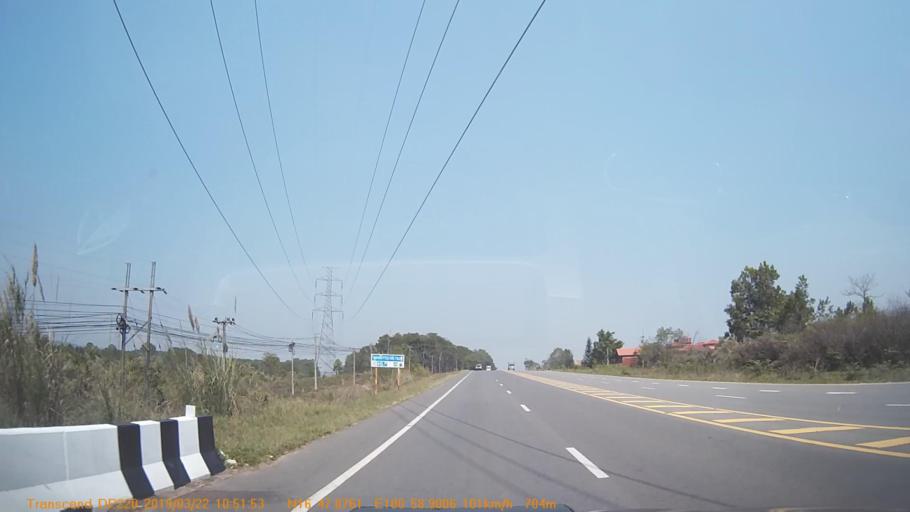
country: TH
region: Phetchabun
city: Khao Kho
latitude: 16.7982
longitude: 100.9815
